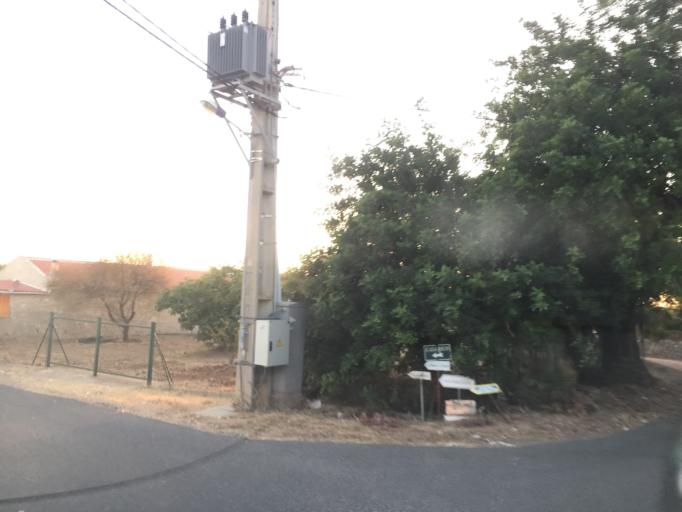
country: PT
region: Faro
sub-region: Loule
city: Almancil
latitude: 37.1082
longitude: -8.0076
